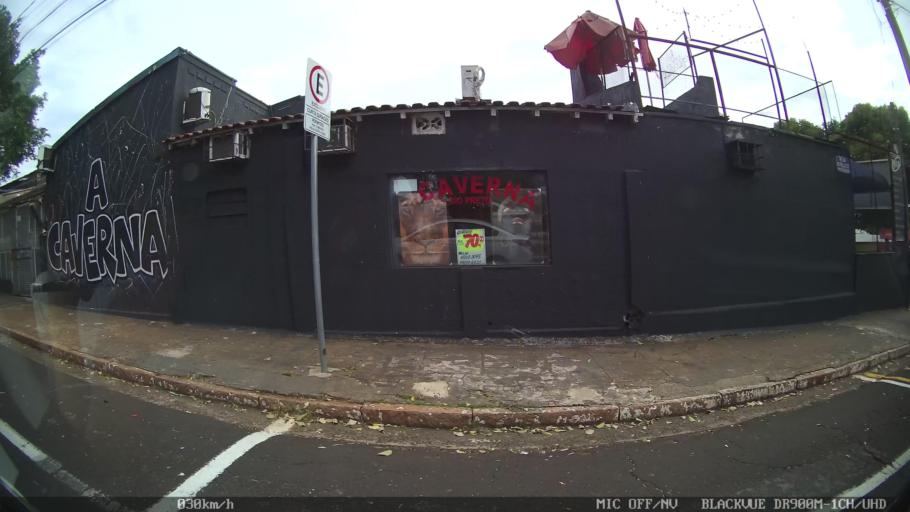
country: BR
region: Sao Paulo
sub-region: Sao Jose Do Rio Preto
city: Sao Jose do Rio Preto
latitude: -20.8171
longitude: -49.3721
